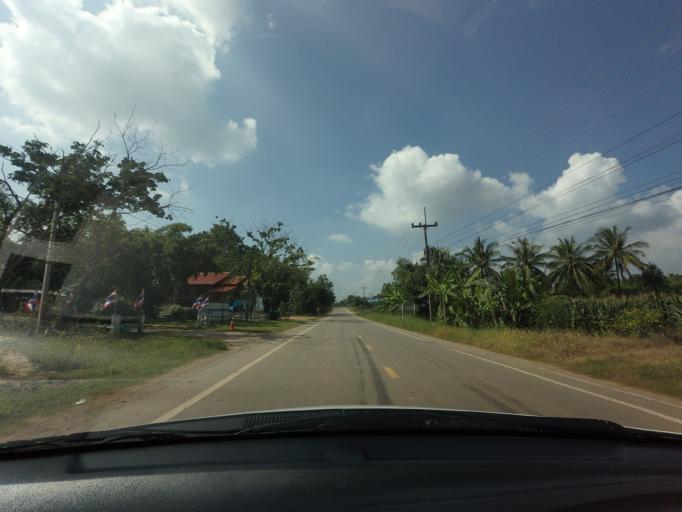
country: TH
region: Nakhon Ratchasima
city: Wang Nam Khiao
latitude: 14.4450
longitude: 101.6730
